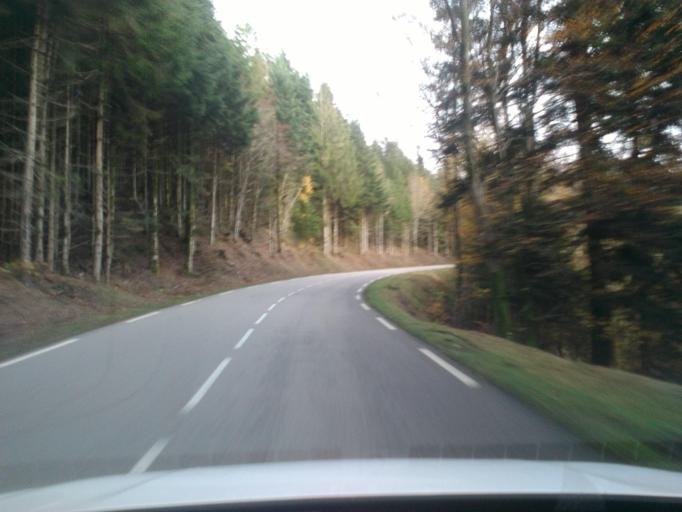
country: FR
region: Lorraine
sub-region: Departement des Vosges
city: Senones
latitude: 48.4052
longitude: 7.0827
